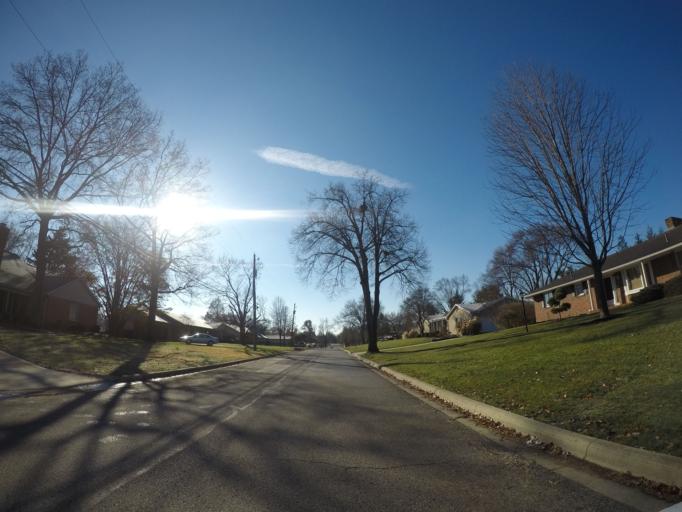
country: US
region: Ohio
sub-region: Franklin County
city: Upper Arlington
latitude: 40.0360
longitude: -83.0632
